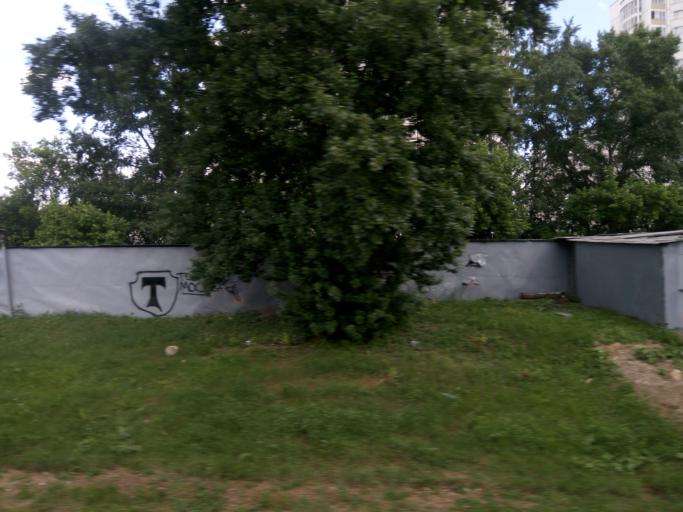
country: RU
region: Moscow
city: Novyye Cheremushki
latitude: 55.6930
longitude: 37.6158
